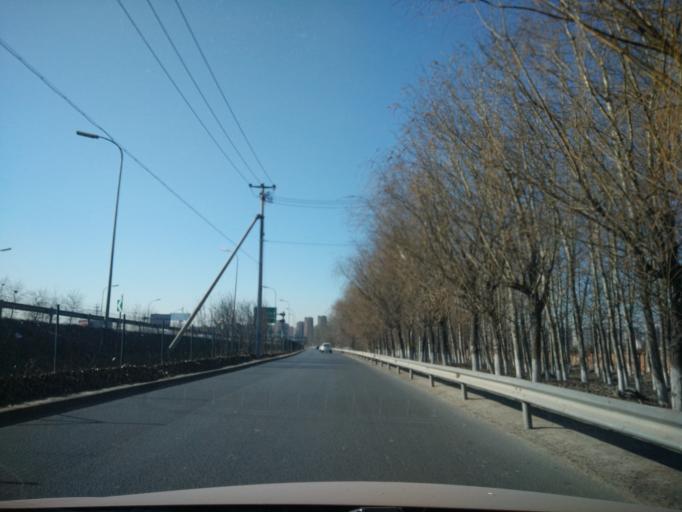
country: CN
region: Beijing
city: Jiugong
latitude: 39.7891
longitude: 116.4324
